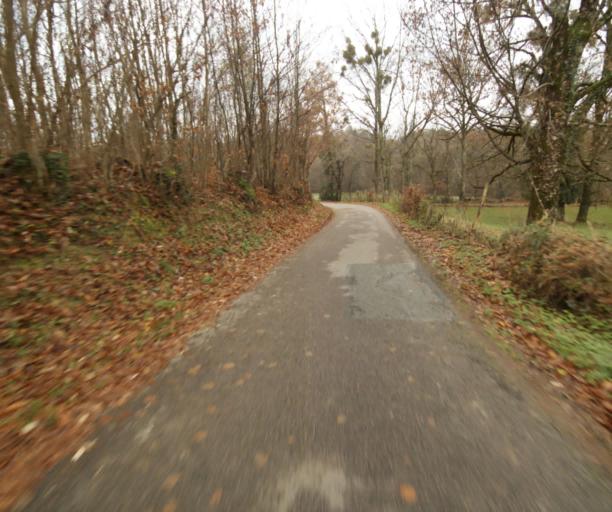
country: FR
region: Limousin
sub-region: Departement de la Correze
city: Laguenne
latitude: 45.2344
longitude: 1.7427
